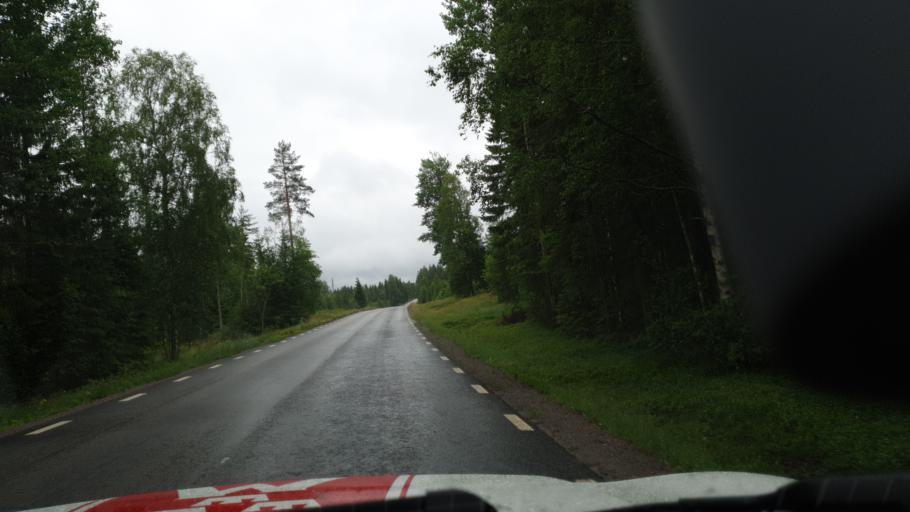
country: SE
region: Vaesterbotten
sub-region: Vannas Kommun
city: Vannasby
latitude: 63.8016
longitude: 19.8494
